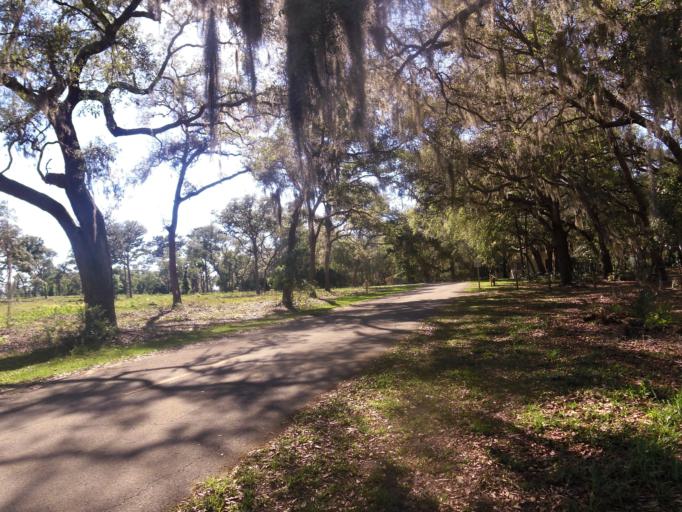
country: US
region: Florida
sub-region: Clay County
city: Keystone Heights
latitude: 29.8232
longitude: -81.9449
